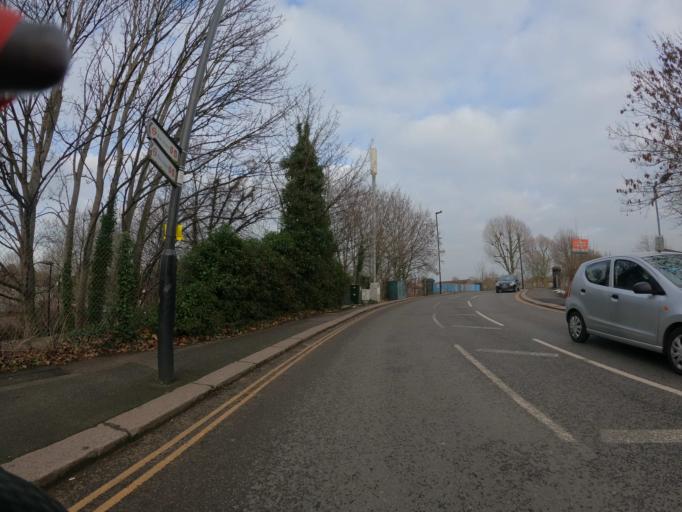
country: GB
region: England
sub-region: Greater London
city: Greenford
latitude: 51.5167
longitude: -0.3307
